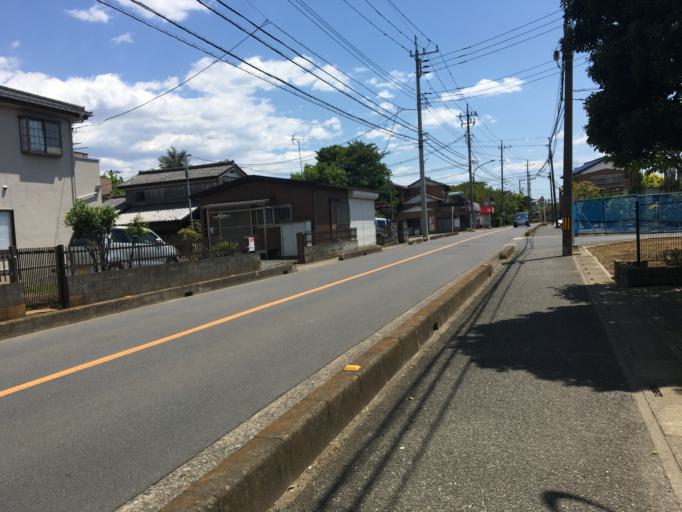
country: JP
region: Saitama
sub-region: Kawaguchi-shi
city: Hatogaya-honcho
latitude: 35.8464
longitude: 139.7531
